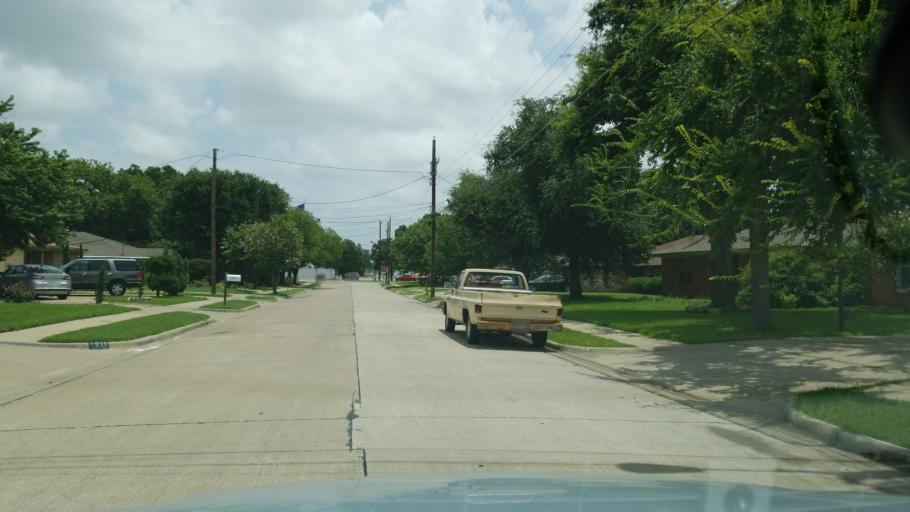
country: US
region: Texas
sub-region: Dallas County
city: Irving
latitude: 32.8277
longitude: -96.9205
